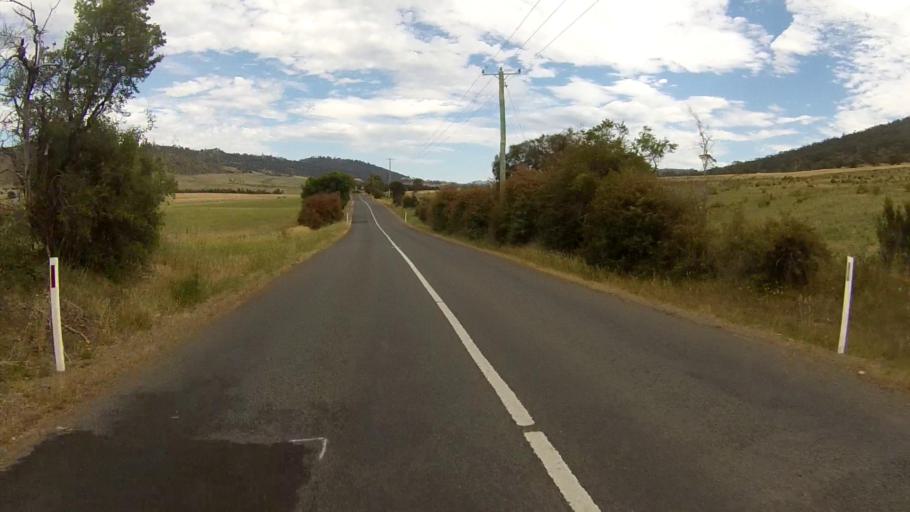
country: AU
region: Tasmania
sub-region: Clarence
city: Cambridge
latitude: -42.7325
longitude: 147.4070
